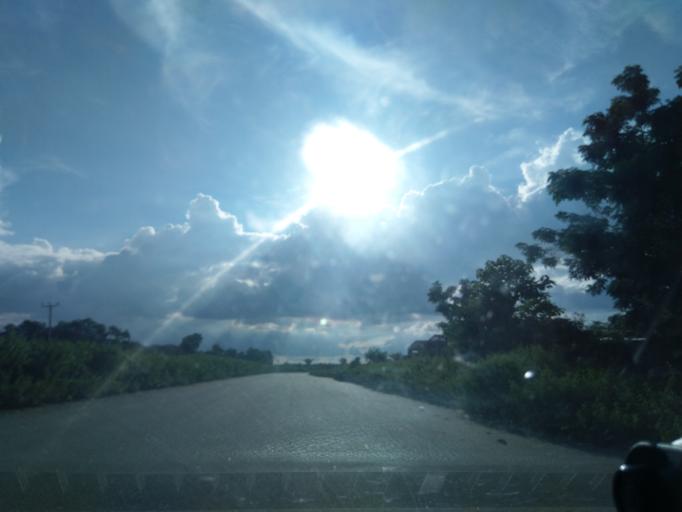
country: NG
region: Abuja Federal Capital Territory
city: Abuja
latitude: 9.0299
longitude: 7.3962
